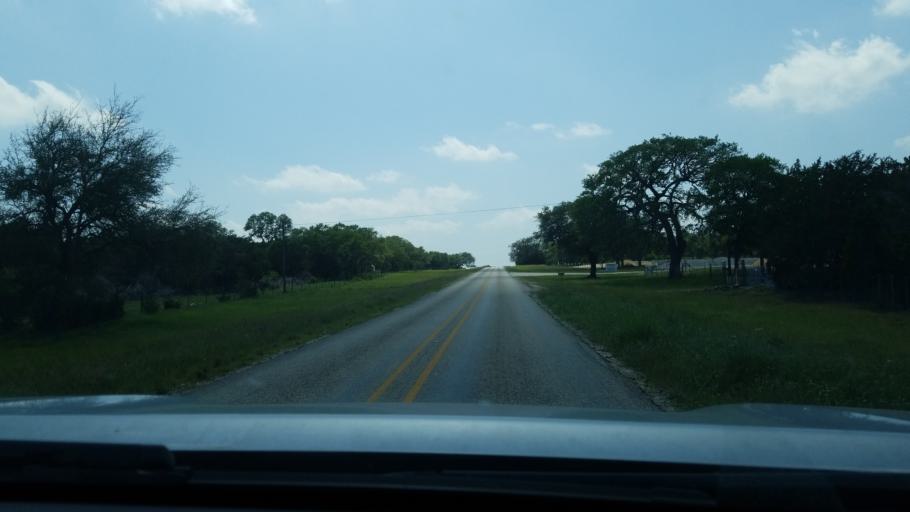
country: US
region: Texas
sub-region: Blanco County
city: Blanco
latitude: 29.9555
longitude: -98.5469
